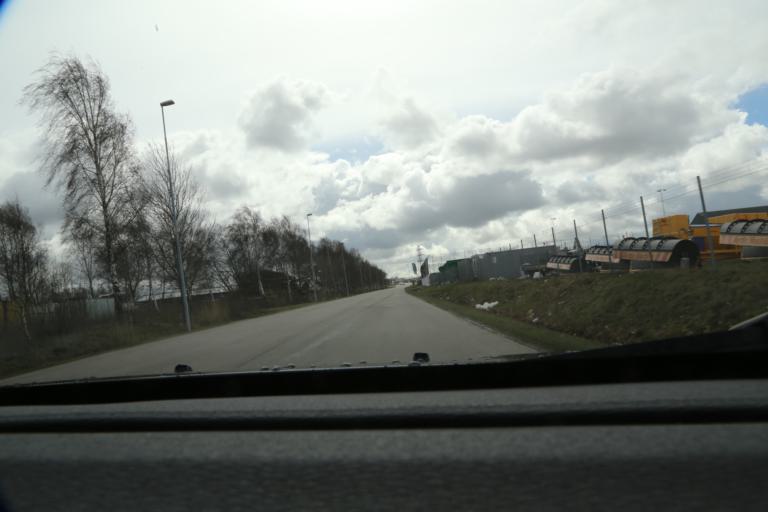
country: SE
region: Halland
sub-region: Varbergs Kommun
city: Varberg
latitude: 57.1276
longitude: 12.2857
